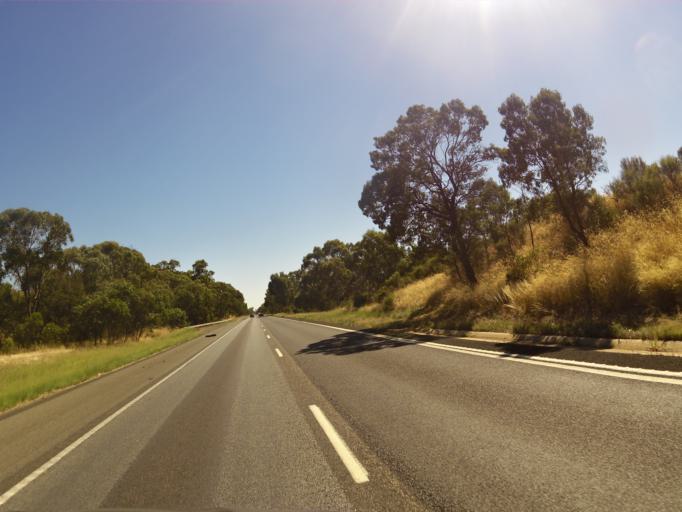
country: AU
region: Victoria
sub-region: Greater Shepparton
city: Shepparton
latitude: -36.8922
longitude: 145.2601
